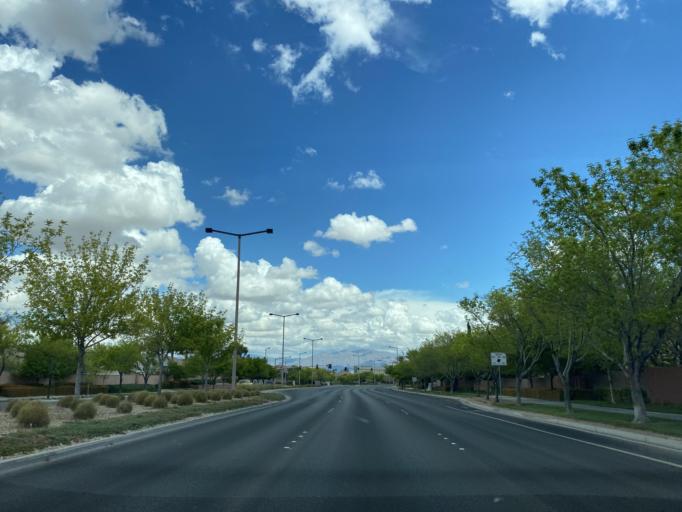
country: US
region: Nevada
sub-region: Clark County
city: Summerlin South
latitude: 36.1730
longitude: -115.3237
